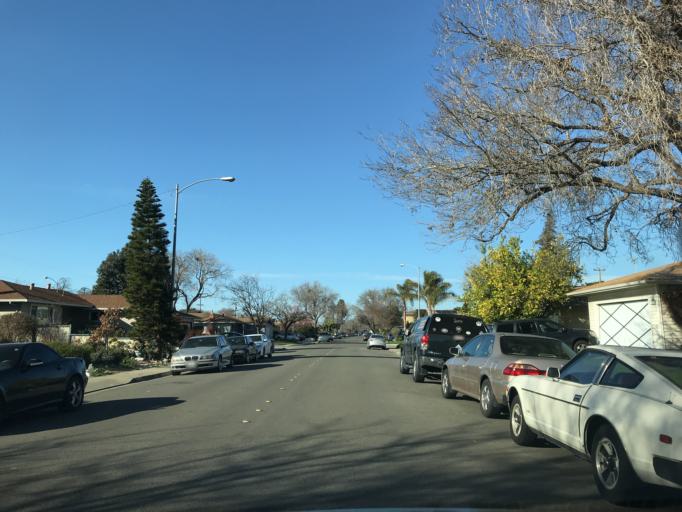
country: US
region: California
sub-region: Santa Clara County
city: Milpitas
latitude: 37.4304
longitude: -121.9163
